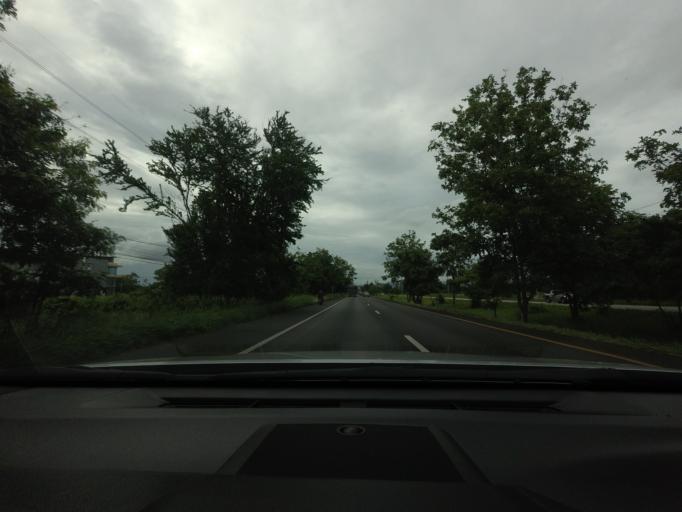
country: TH
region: Prachuap Khiri Khan
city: Hua Hin
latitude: 12.6259
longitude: 99.8579
